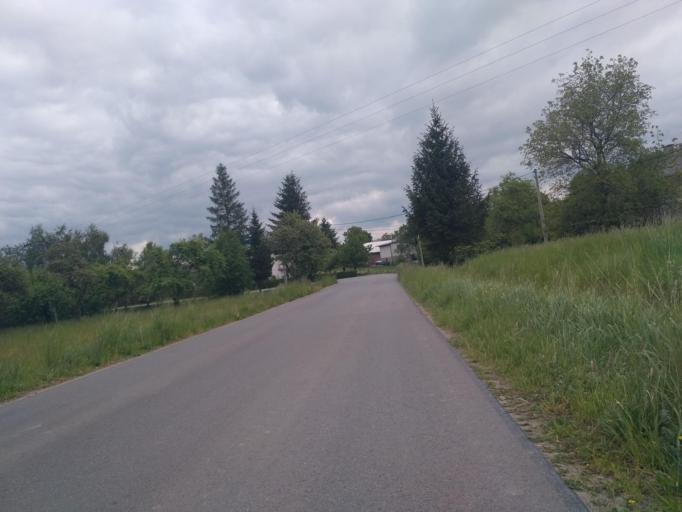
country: PL
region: Subcarpathian Voivodeship
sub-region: Powiat jasielski
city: Tarnowiec
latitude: 49.7116
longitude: 21.5964
